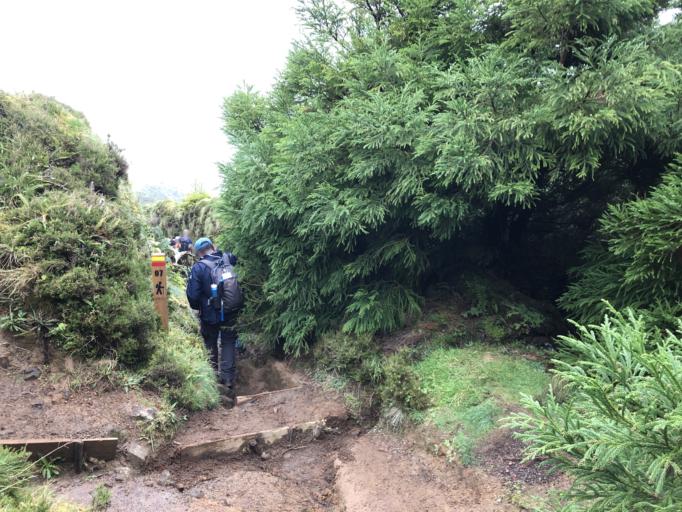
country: PT
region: Azores
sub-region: Ponta Delgada
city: Arrifes
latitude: 37.8311
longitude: -25.7550
